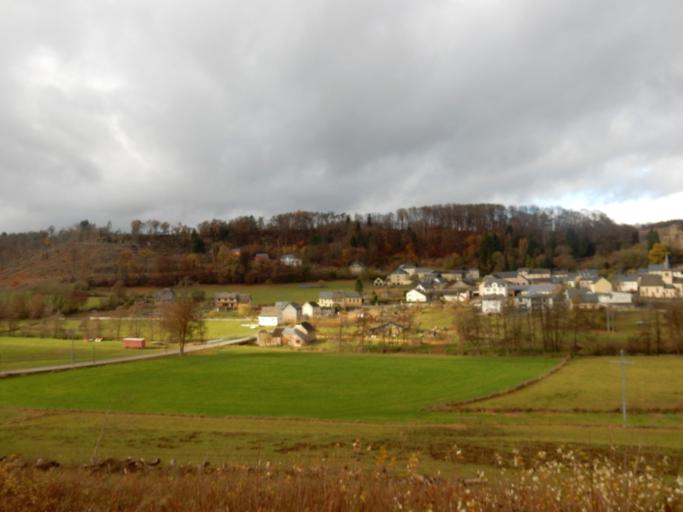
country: LU
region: Luxembourg
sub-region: Canton de Capellen
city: Septfontaines
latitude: 49.6969
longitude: 5.9674
